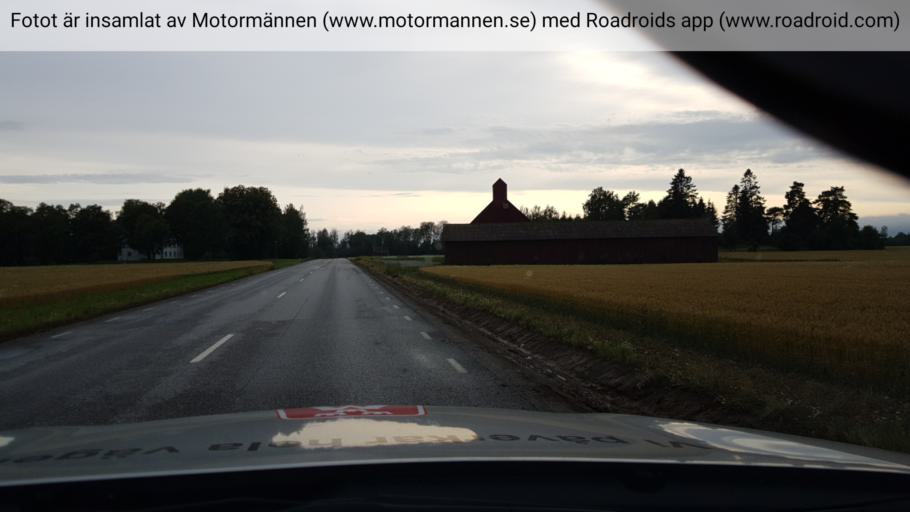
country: SE
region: Vaestmanland
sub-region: Vasteras
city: Skultuna
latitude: 59.7882
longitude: 16.4750
